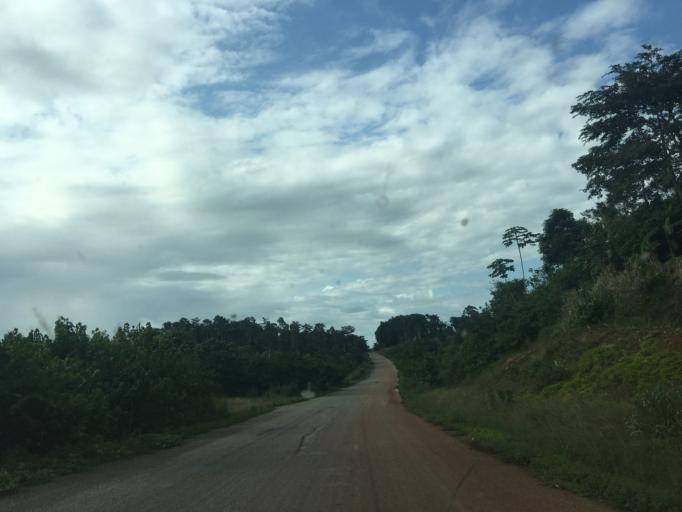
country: GH
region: Western
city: Wassa-Akropong
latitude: 5.9868
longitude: -2.4129
